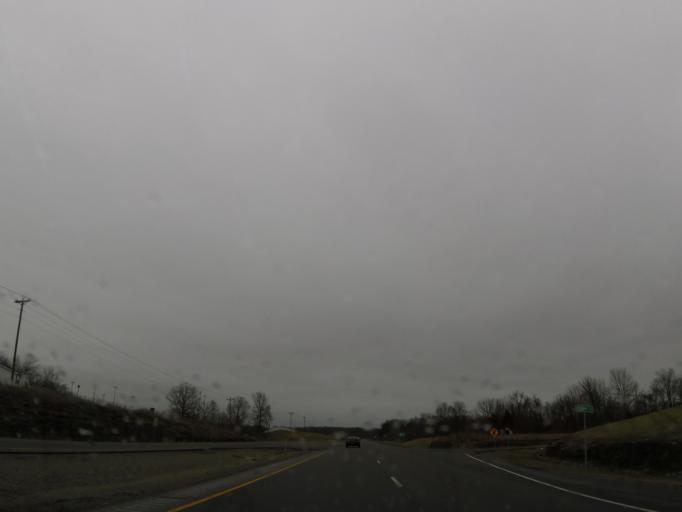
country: US
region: Kentucky
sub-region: Lincoln County
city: Stanford
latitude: 37.5400
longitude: -84.6507
